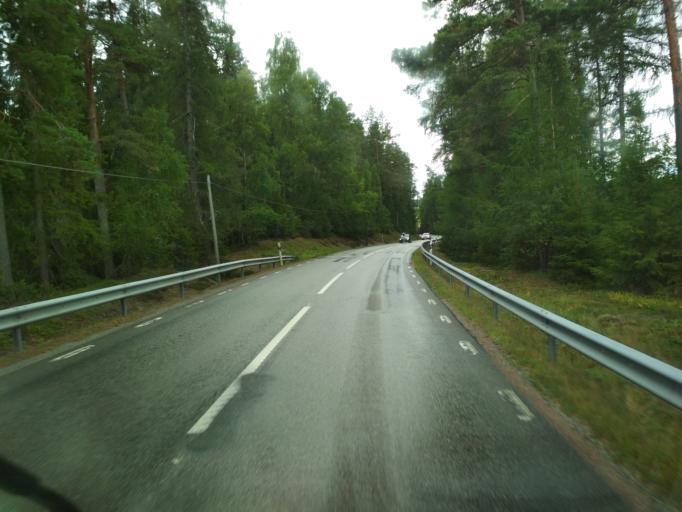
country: SE
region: Vaestmanland
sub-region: Surahammars Kommun
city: Surahammar
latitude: 59.7187
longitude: 16.1978
